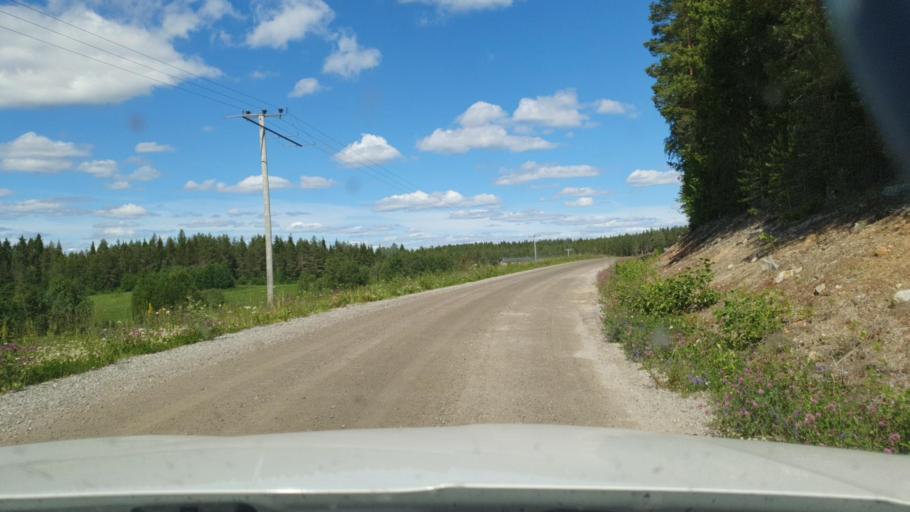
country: SE
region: Vaesterbotten
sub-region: Skelleftea Kommun
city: Backa
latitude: 65.1463
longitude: 21.1673
